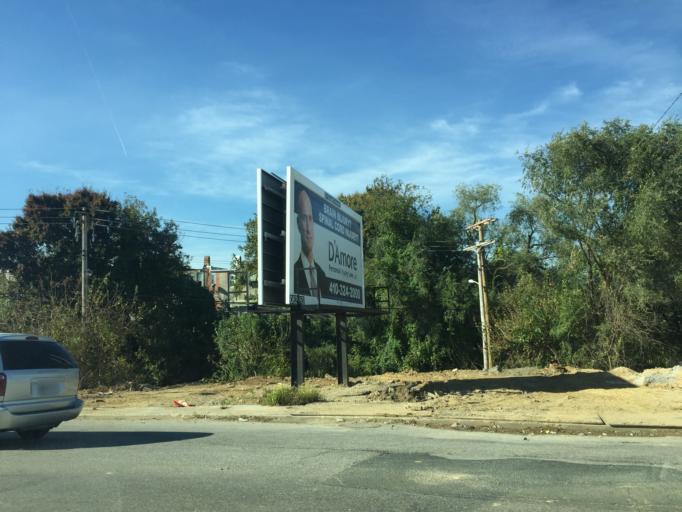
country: US
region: Maryland
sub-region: City of Baltimore
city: Baltimore
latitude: 39.2892
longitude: -76.6556
